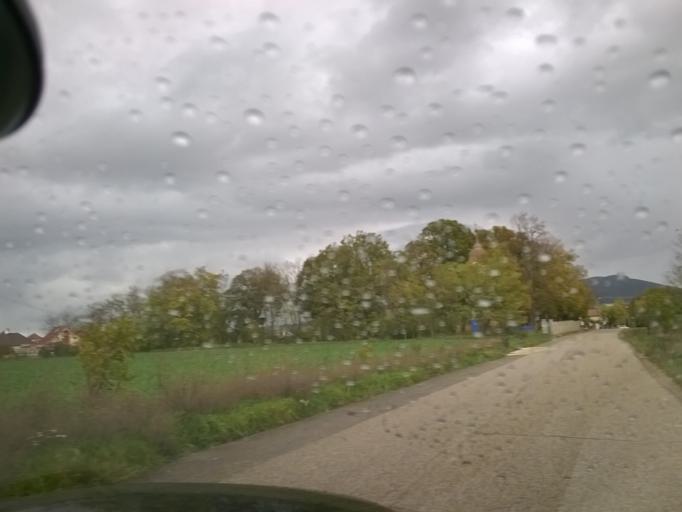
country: SK
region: Nitriansky
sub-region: Okres Nitra
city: Nitra
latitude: 48.3135
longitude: 18.0336
